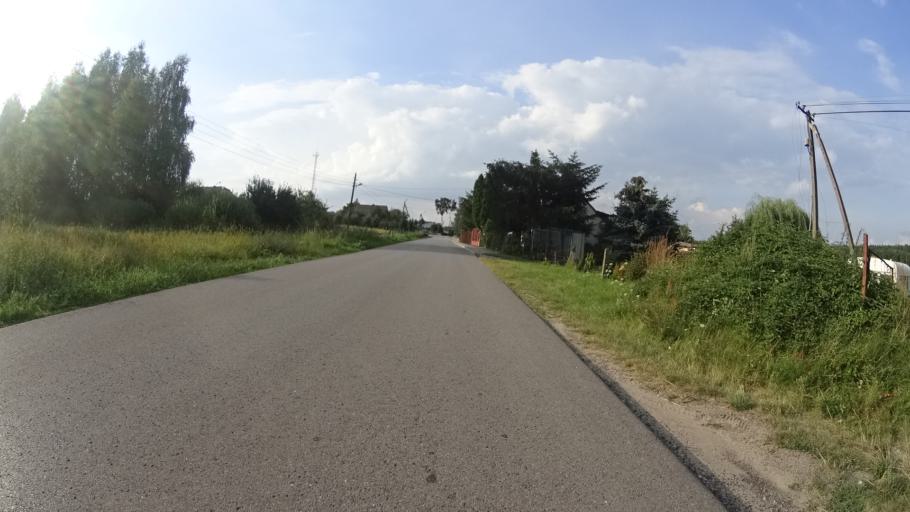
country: PL
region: Masovian Voivodeship
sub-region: Powiat grojecki
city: Mogielnica
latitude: 51.6830
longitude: 20.7317
